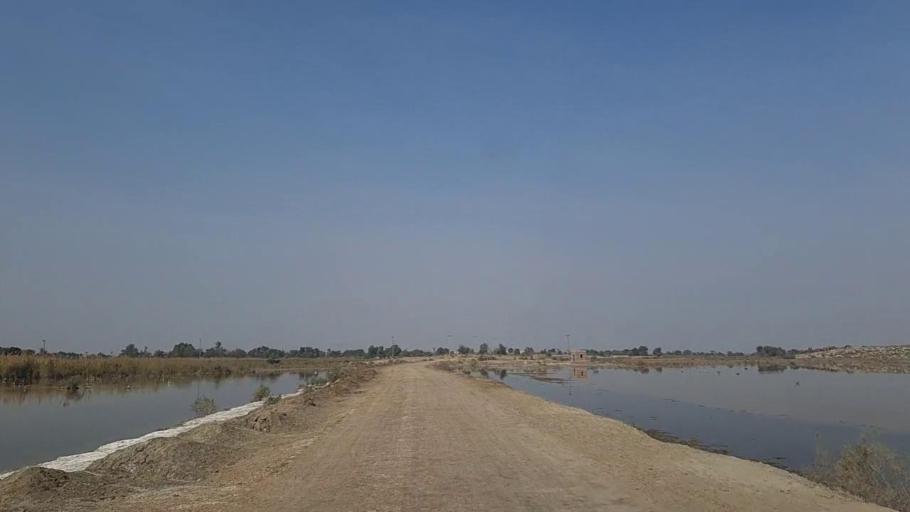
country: PK
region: Sindh
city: Daur
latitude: 26.5078
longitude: 68.4795
